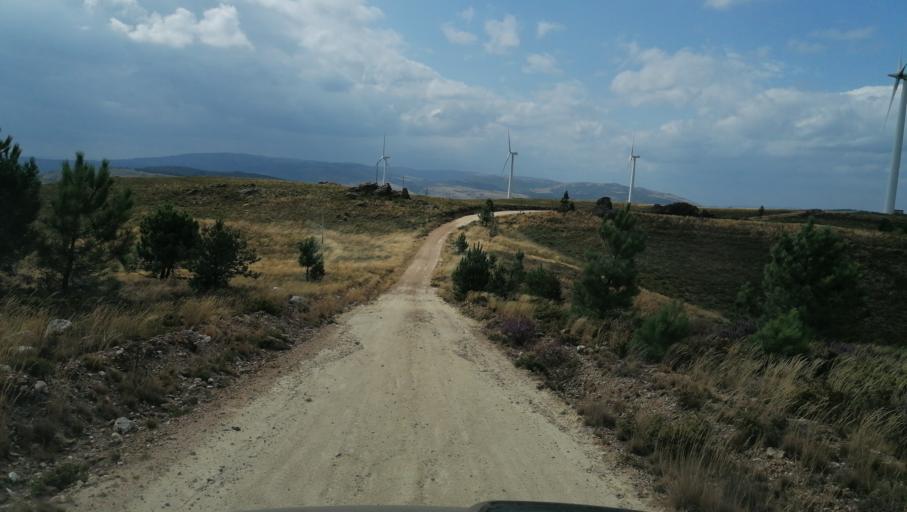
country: PT
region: Vila Real
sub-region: Vila Pouca de Aguiar
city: Vila Pouca de Aguiar
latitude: 41.5340
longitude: -7.7158
